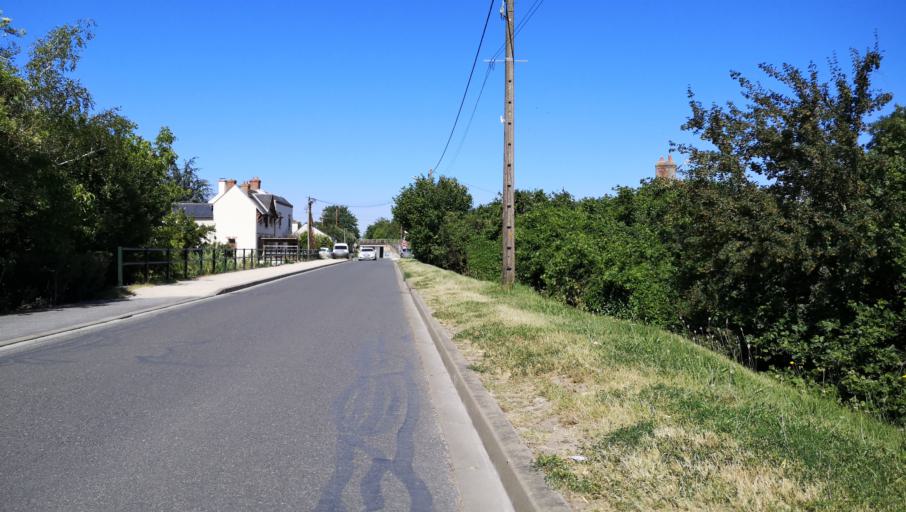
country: FR
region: Centre
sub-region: Departement du Loiret
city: Saint-Jean-le-Blanc
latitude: 47.8928
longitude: 1.9254
